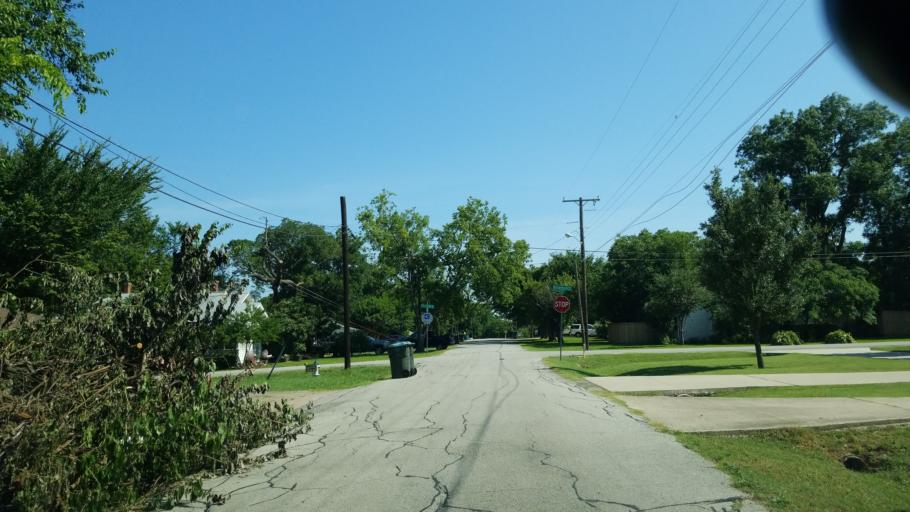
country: US
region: Texas
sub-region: Dallas County
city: Carrollton
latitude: 32.9560
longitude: -96.9002
